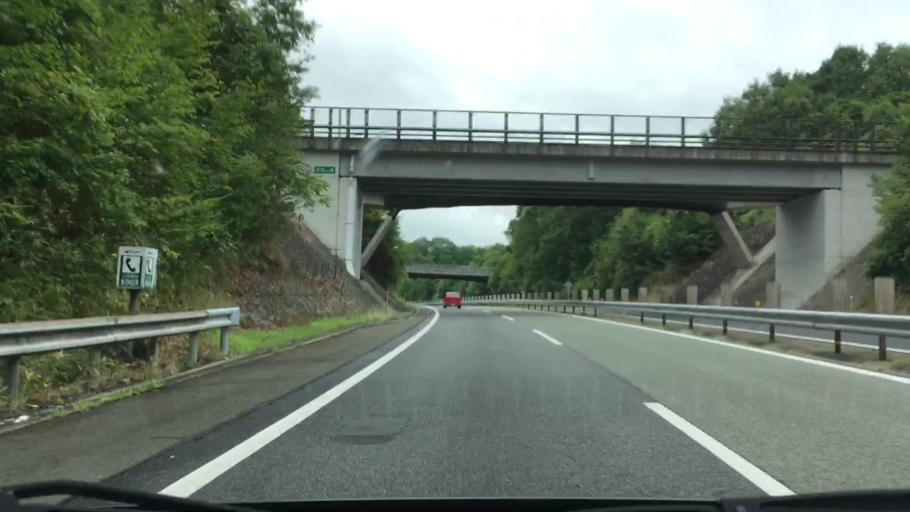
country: JP
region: Hiroshima
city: Shobara
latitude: 34.8463
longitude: 133.0126
